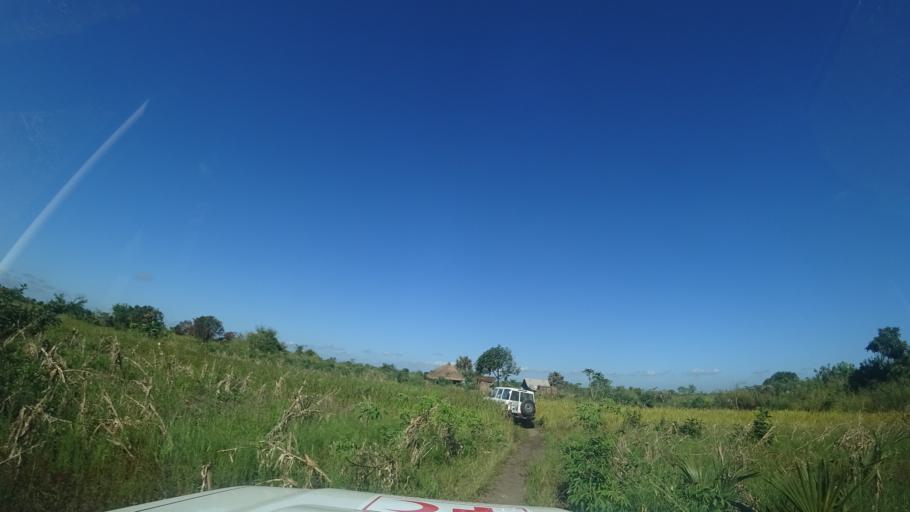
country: MZ
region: Sofala
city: Dondo
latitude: -19.3980
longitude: 34.5949
